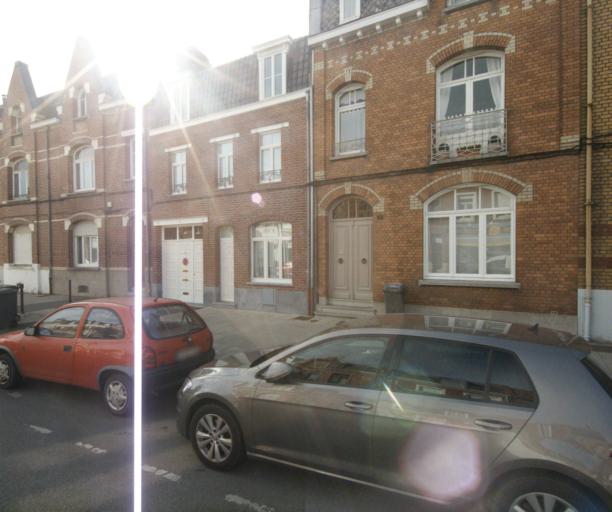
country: FR
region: Nord-Pas-de-Calais
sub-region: Departement du Nord
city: La Bassee
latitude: 50.5294
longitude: 2.8022
